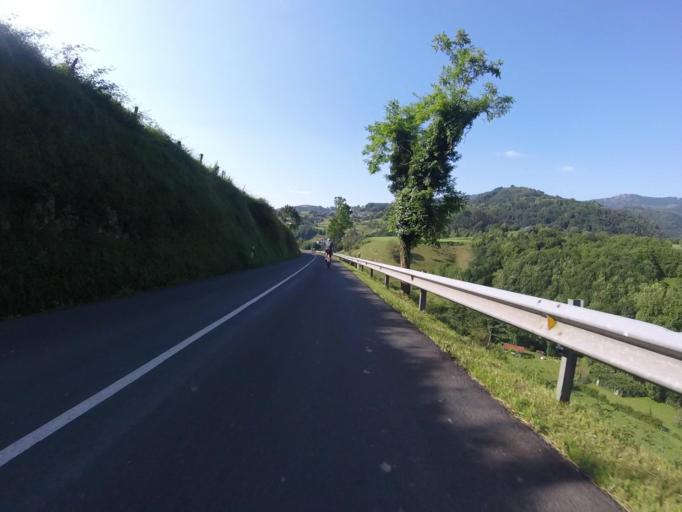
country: ES
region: Basque Country
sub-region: Provincia de Guipuzcoa
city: Asteasu
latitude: 43.1990
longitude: -2.1031
